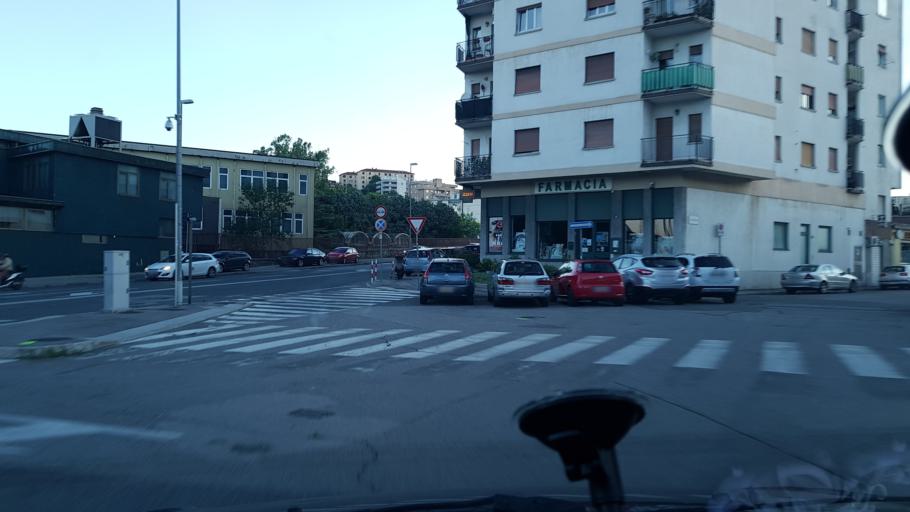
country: IT
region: Friuli Venezia Giulia
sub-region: Provincia di Trieste
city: Trieste
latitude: 45.6257
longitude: 13.7953
